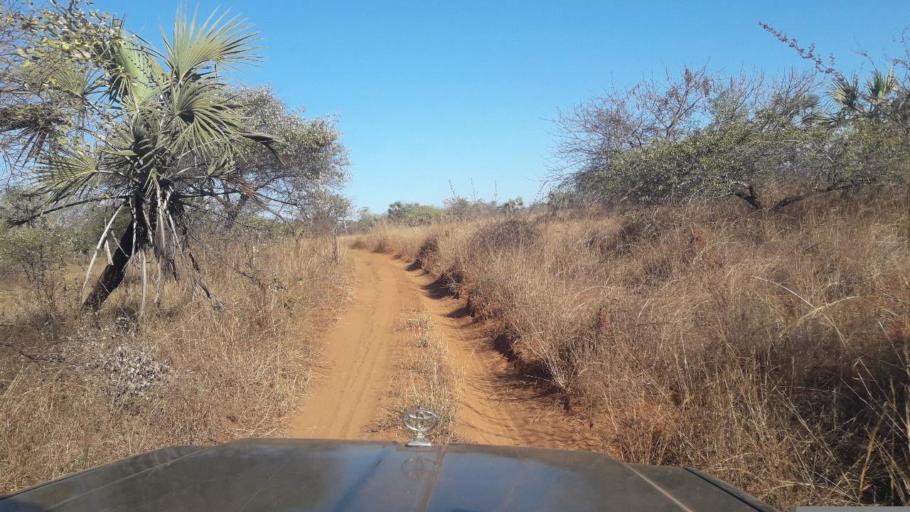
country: MG
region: Boeny
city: Sitampiky
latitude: -16.4115
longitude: 45.6028
